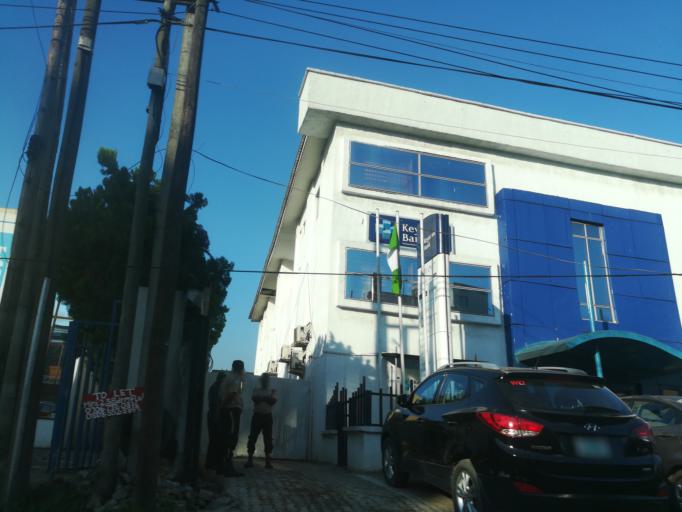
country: NG
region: Lagos
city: Ikeja
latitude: 6.5968
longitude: 3.3547
